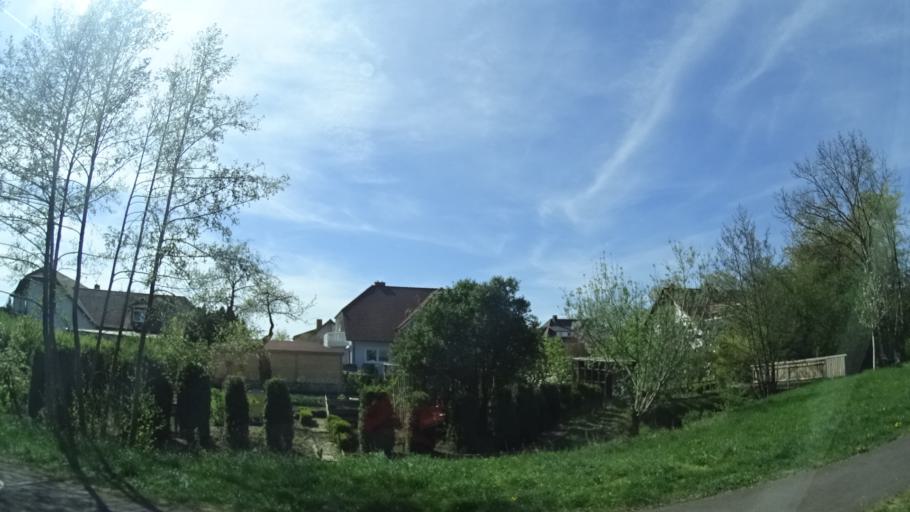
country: DE
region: Bavaria
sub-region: Regierungsbezirk Unterfranken
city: Hofheim in Unterfranken
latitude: 50.1409
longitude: 10.5310
